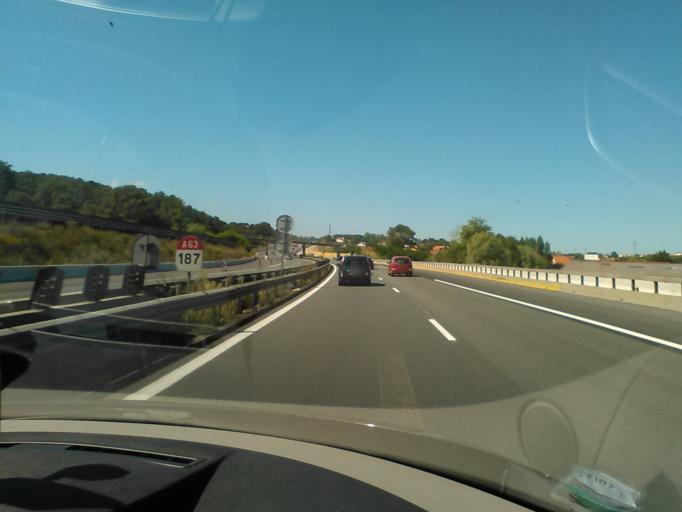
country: FR
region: Aquitaine
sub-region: Departement des Pyrenees-Atlantiques
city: Bidart
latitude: 43.4301
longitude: -1.5850
